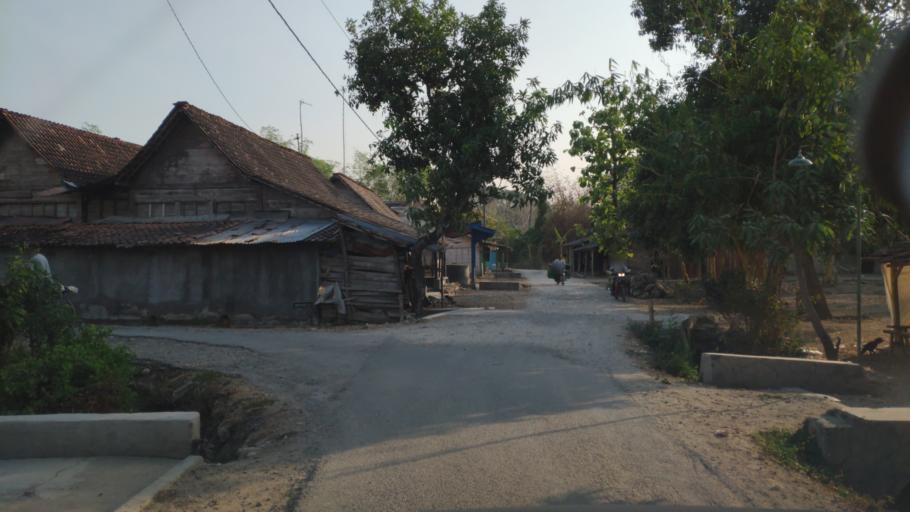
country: ID
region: Central Java
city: Jepang Satu
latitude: -7.0175
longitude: 111.4240
